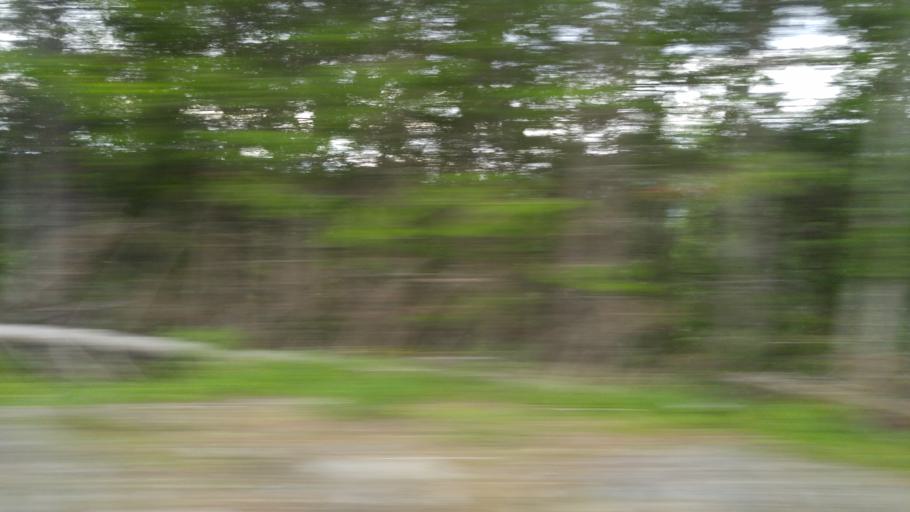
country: NO
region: Nord-Trondelag
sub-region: Meraker
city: Meraker
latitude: 63.4075
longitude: 11.7626
